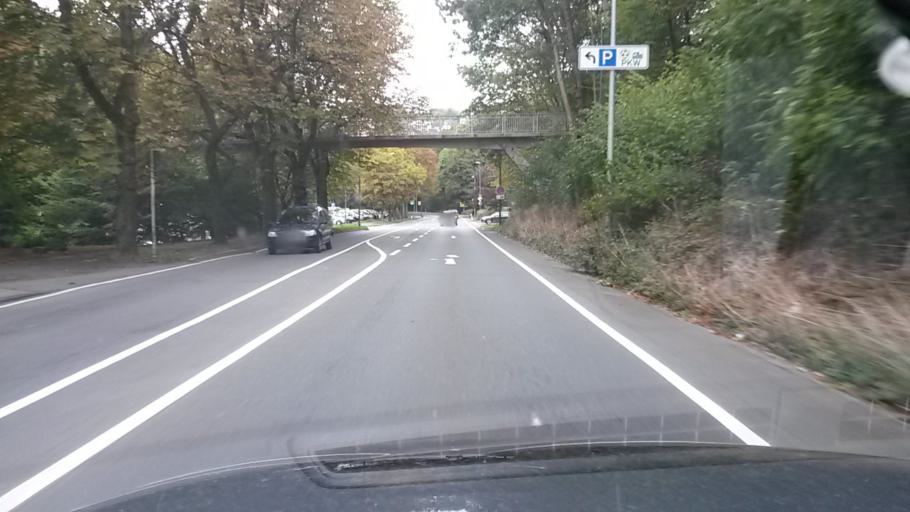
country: DE
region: North Rhine-Westphalia
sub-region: Regierungsbezirk Arnsberg
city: Luedenscheid
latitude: 51.2100
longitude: 7.6208
